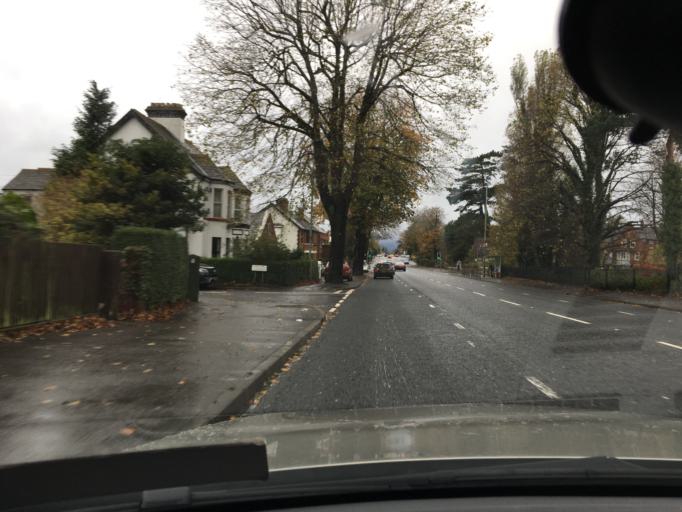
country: GB
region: Northern Ireland
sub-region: Castlereagh District
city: Castlereagh
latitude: 54.5944
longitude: -5.8478
